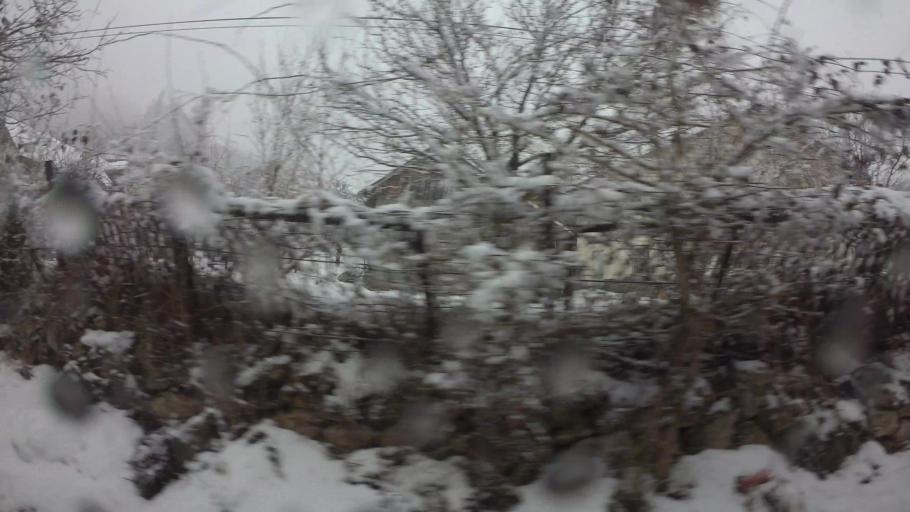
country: BA
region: Federation of Bosnia and Herzegovina
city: Kobilja Glava
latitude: 43.8535
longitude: 18.4490
